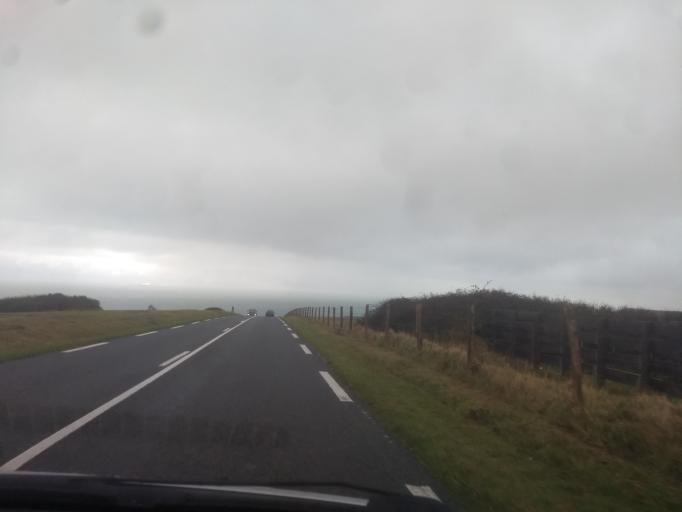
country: FR
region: Nord-Pas-de-Calais
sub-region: Departement du Pas-de-Calais
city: Sangatte
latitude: 50.9285
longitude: 1.7202
